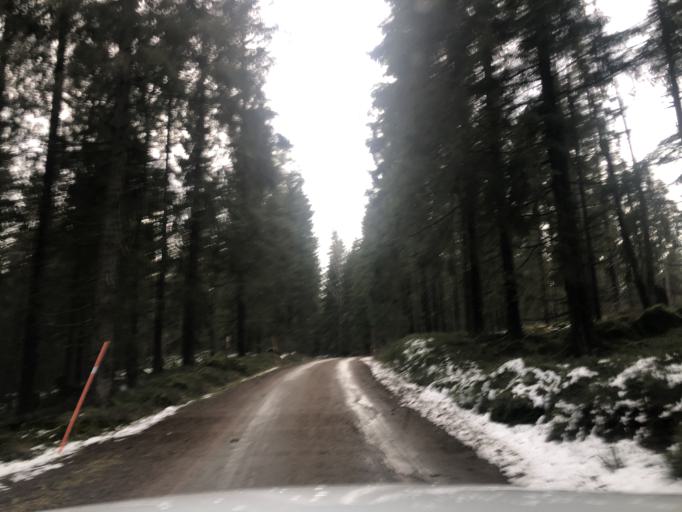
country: SE
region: Vaestra Goetaland
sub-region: Ulricehamns Kommun
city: Ulricehamn
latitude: 57.7828
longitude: 13.4796
